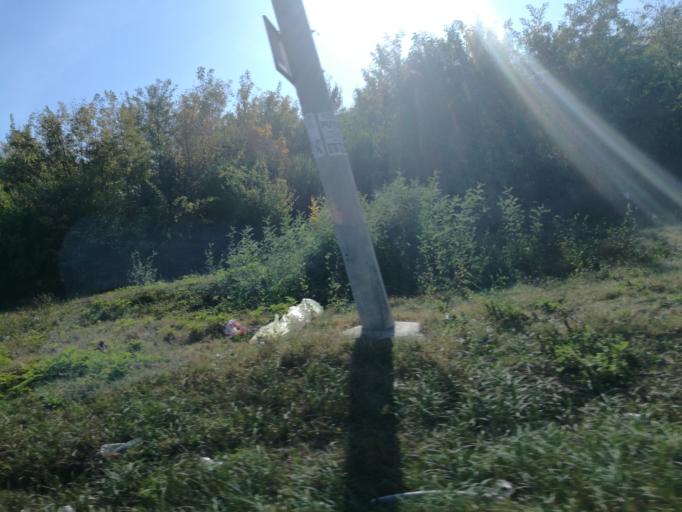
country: RO
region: Ilfov
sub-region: Comuna Dragomiresti-Vale
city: Dragomiresti-Vale
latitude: 44.4701
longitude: 25.9184
